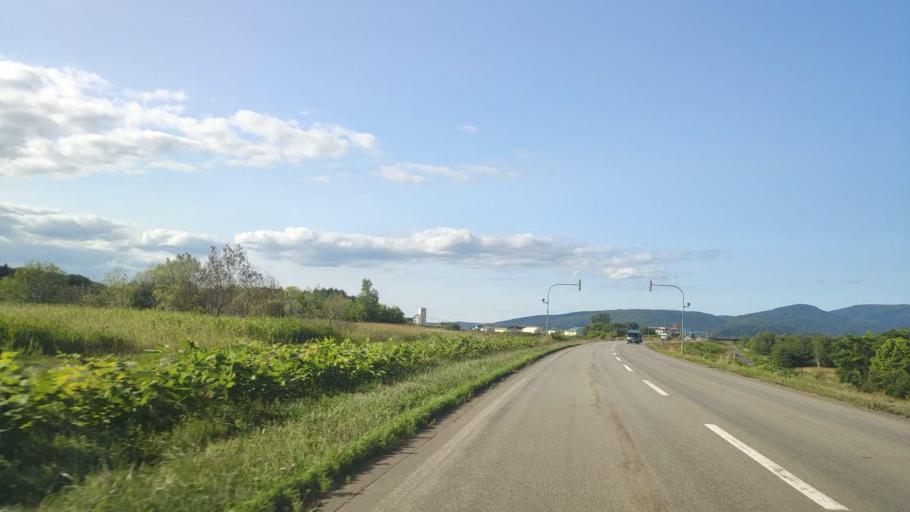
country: JP
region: Hokkaido
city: Nayoro
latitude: 44.8120
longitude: 142.0659
